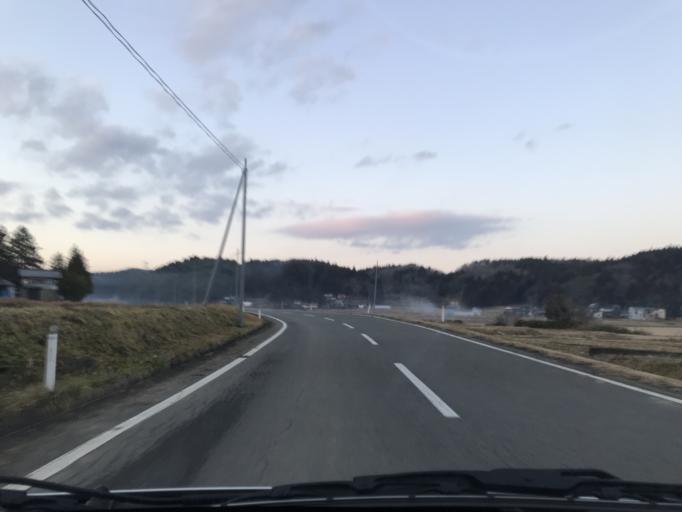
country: JP
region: Iwate
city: Ichinoseki
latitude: 38.8391
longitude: 141.1284
